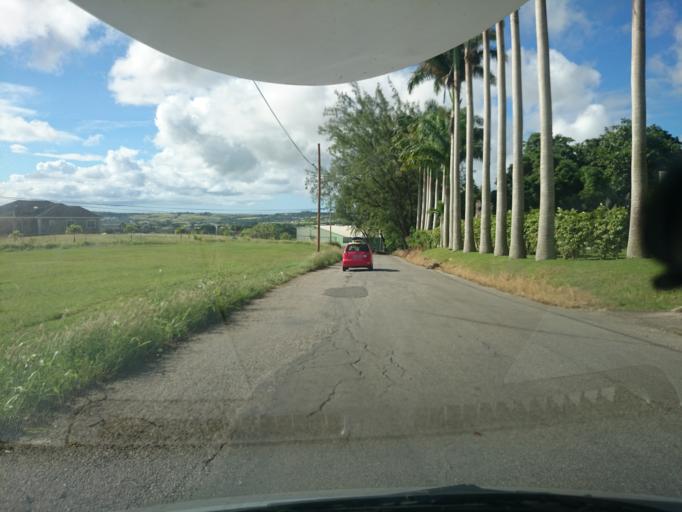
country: BB
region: Saint Thomas
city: Welchman Hall
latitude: 13.1584
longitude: -59.5522
